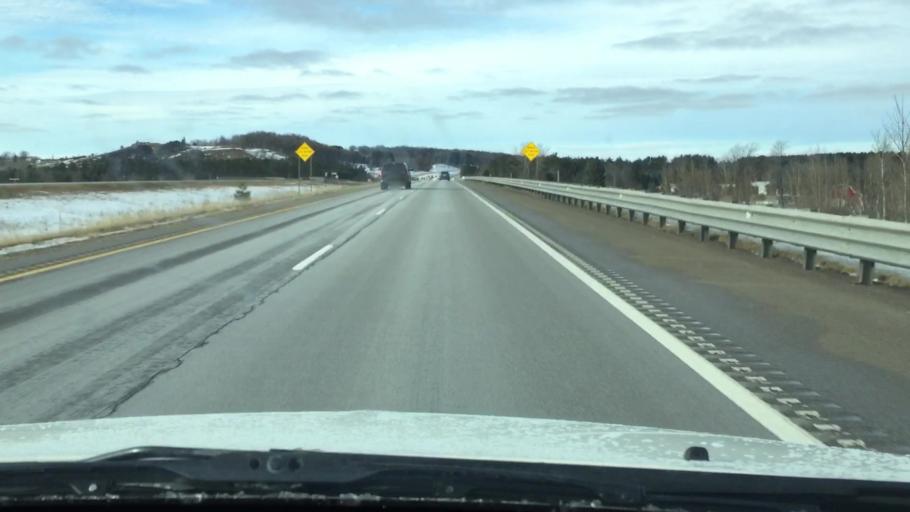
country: US
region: Michigan
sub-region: Wexford County
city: Manton
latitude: 44.4267
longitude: -85.3868
